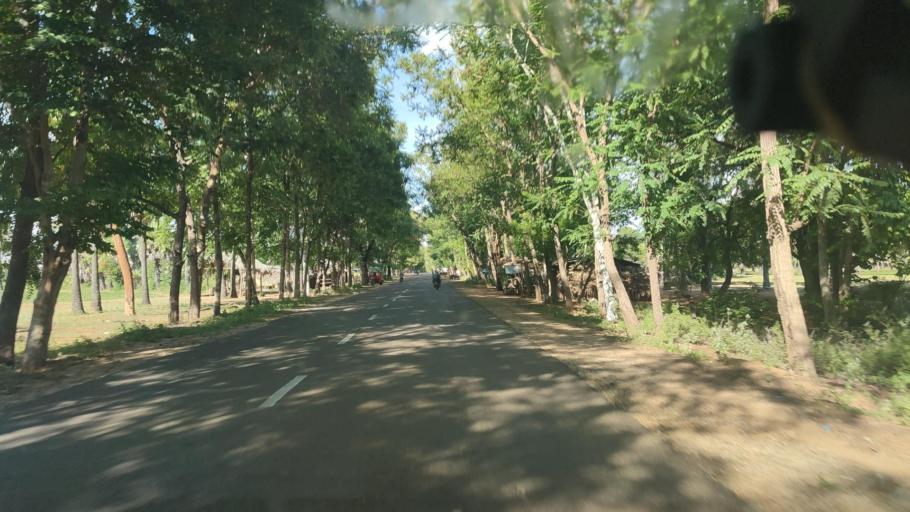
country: MM
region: Magway
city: Chauk
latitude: 20.8412
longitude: 94.8823
